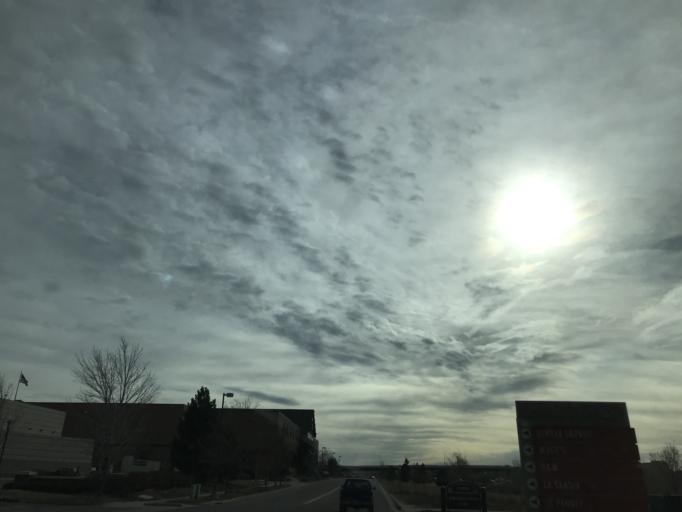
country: US
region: Colorado
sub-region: Adams County
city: Commerce City
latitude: 39.7827
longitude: -104.8964
